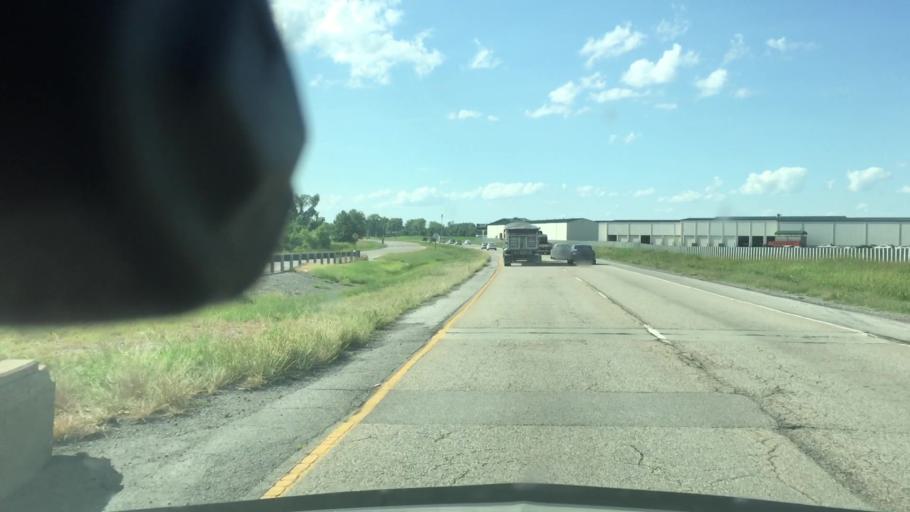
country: US
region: Illinois
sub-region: Madison County
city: Madison
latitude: 38.6569
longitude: -90.1349
